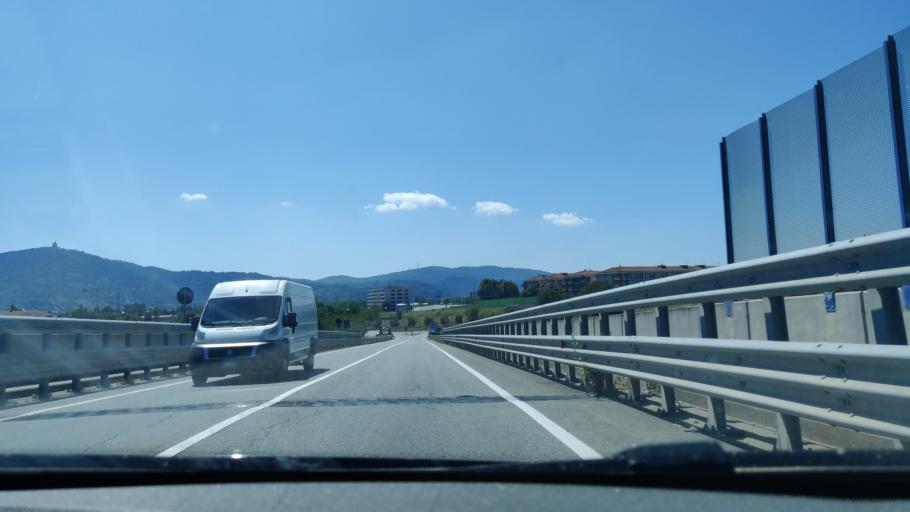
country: IT
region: Piedmont
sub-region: Provincia di Torino
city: Settimo Torinese
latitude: 45.1278
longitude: 7.7325
